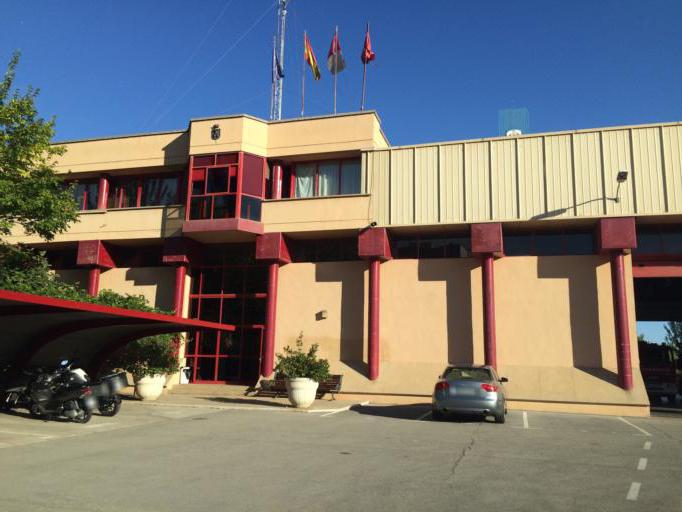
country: ES
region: Castille-La Mancha
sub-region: Provincia de Albacete
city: Albacete
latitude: 39.0043
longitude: -1.8644
